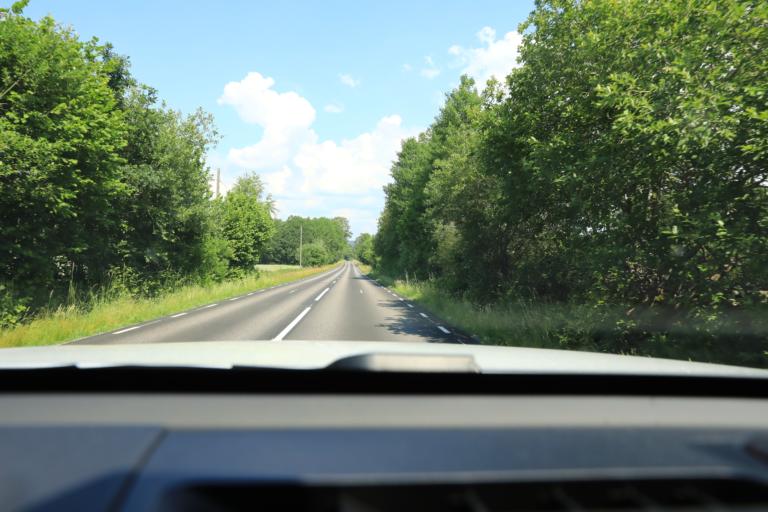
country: SE
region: Halland
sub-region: Varbergs Kommun
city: Veddige
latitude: 57.2037
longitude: 12.2953
